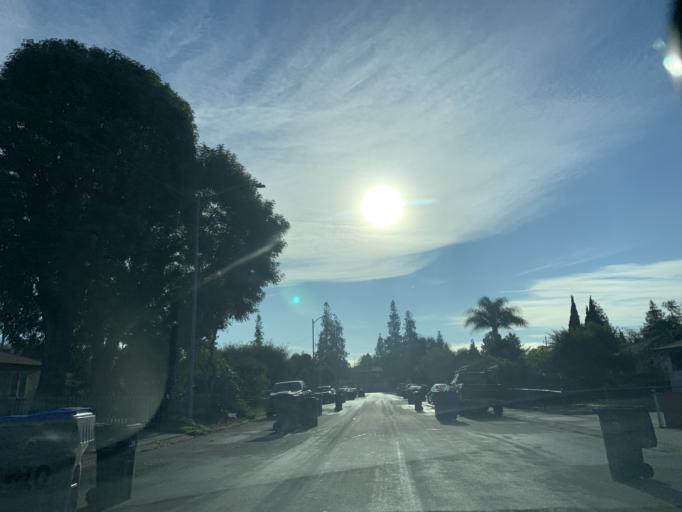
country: US
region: California
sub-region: Santa Clara County
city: San Jose
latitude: 37.3398
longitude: -121.8568
